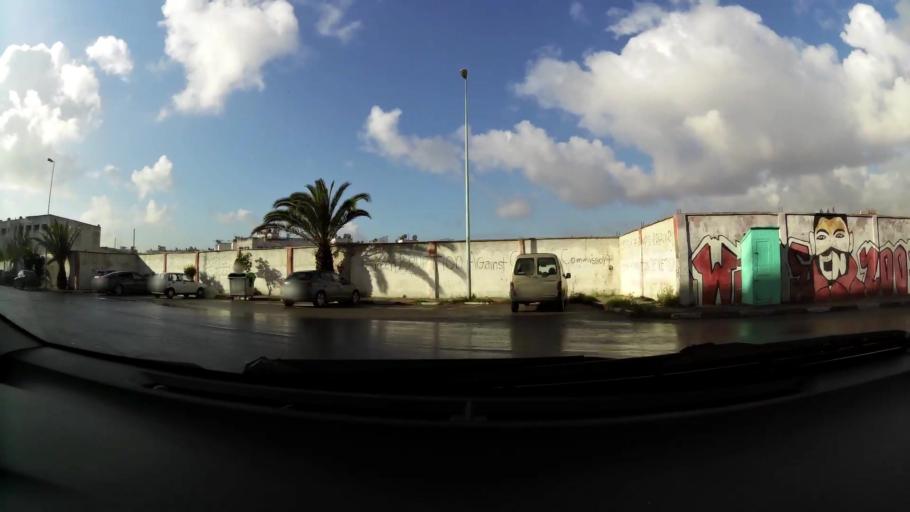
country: MA
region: Grand Casablanca
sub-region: Mediouna
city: Tit Mellil
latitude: 33.5998
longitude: -7.5233
